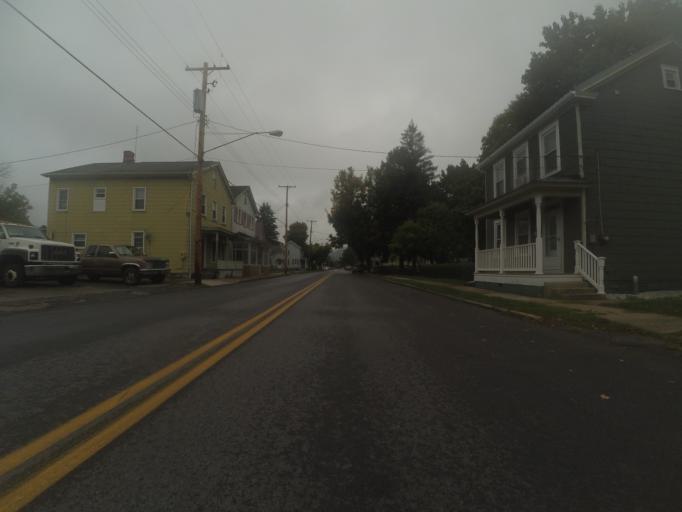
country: US
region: Pennsylvania
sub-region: Huntingdon County
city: McConnellstown
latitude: 40.5590
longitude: -78.1029
